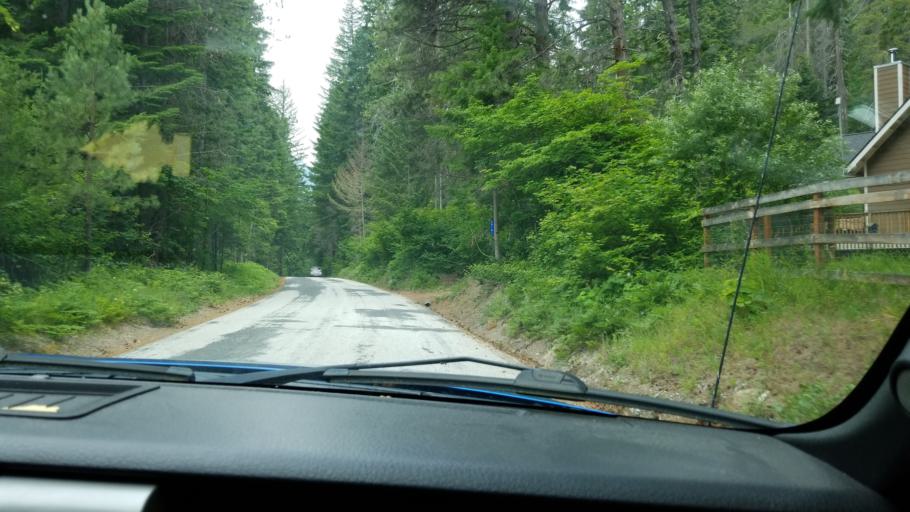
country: US
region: Washington
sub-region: Chelan County
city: Leavenworth
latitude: 47.8584
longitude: -120.8450
